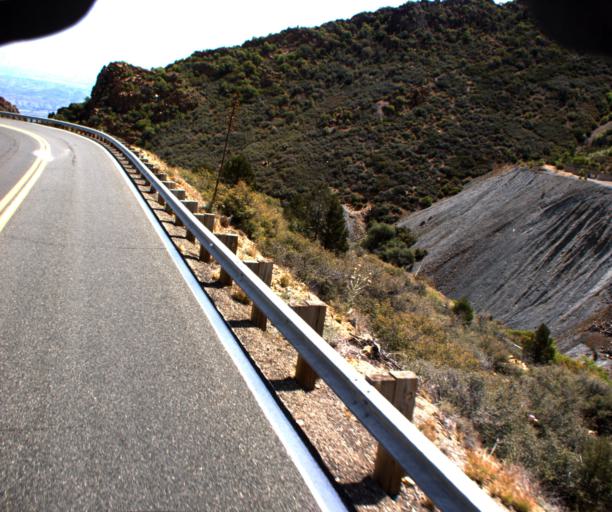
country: US
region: Arizona
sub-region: Yavapai County
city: Clarkdale
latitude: 34.7412
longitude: -112.1236
